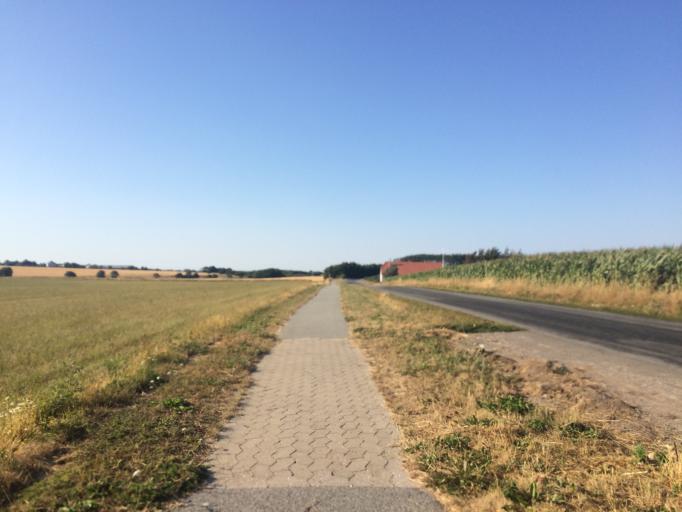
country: DK
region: Central Jutland
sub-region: Holstebro Kommune
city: Vinderup
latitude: 56.6034
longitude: 8.7715
